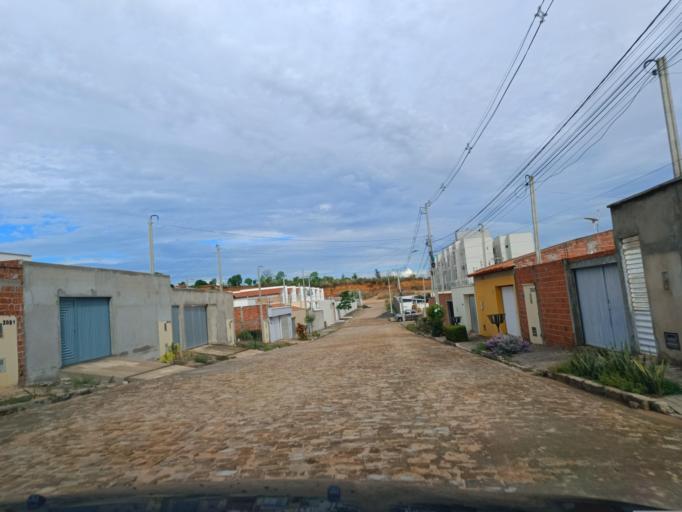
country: BR
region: Piaui
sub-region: Teresina
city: Teresina
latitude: -5.1635
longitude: -42.7771
